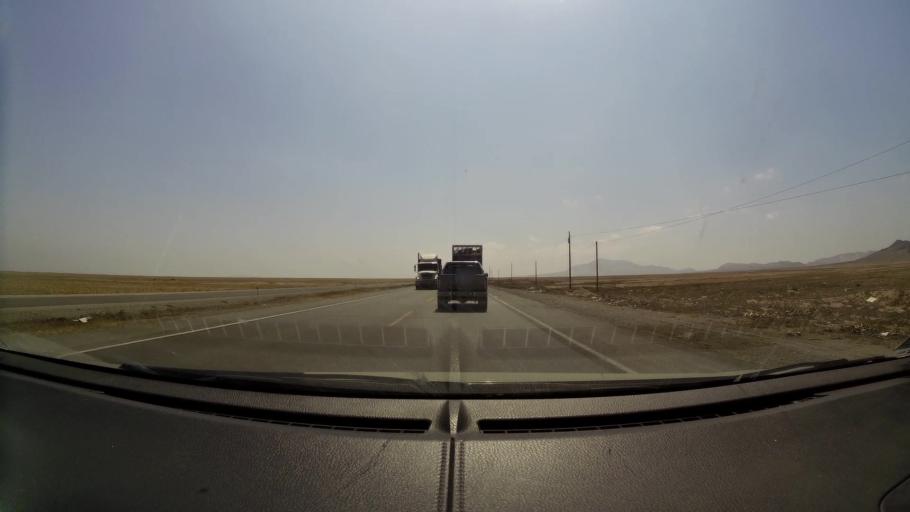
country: PE
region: Lambayeque
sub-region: Provincia de Chiclayo
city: Mocupe
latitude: -6.9545
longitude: -79.6978
